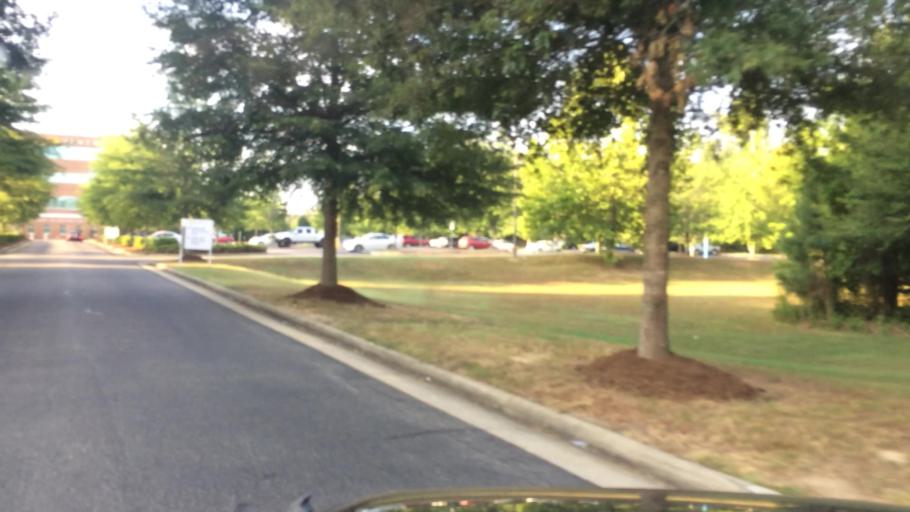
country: US
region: Virginia
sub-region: James City County
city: Williamsburg
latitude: 37.3390
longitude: -76.7423
